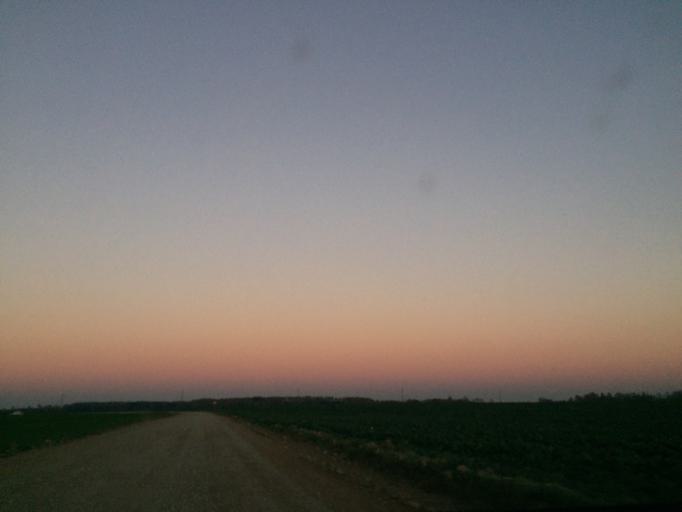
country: LT
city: Akmene
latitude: 56.3857
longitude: 22.7758
